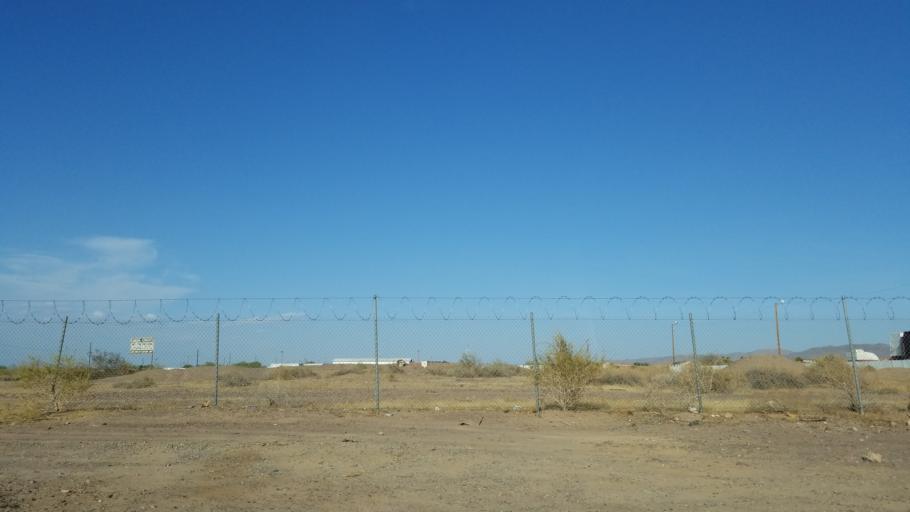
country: US
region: Arizona
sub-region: Maricopa County
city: Laveen
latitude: 33.3898
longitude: -112.2199
